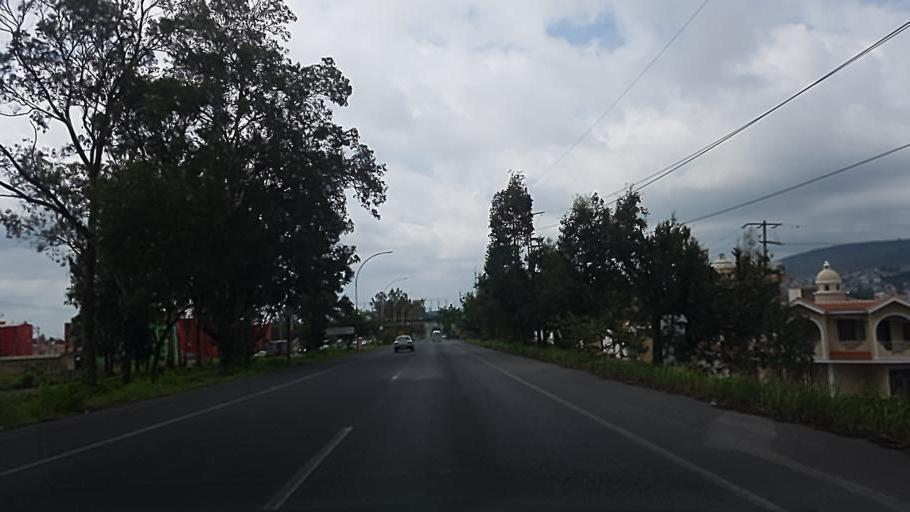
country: MX
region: Nayarit
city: Tepic
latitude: 21.5146
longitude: -104.9244
